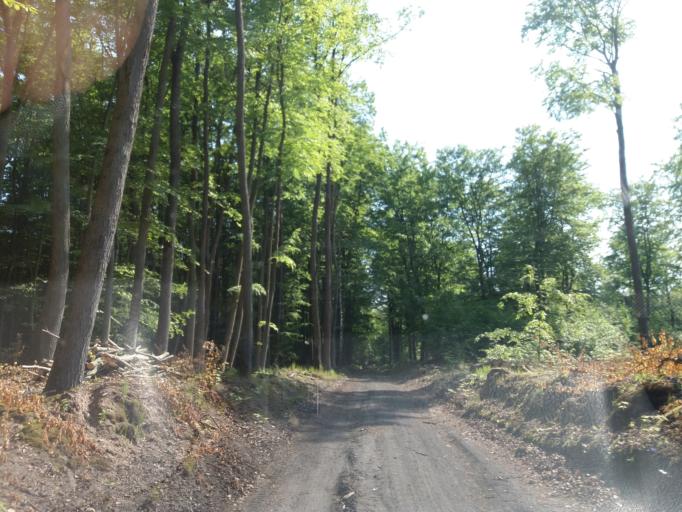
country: PL
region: West Pomeranian Voivodeship
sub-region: Powiat choszczenski
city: Bierzwnik
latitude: 53.0686
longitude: 15.6815
